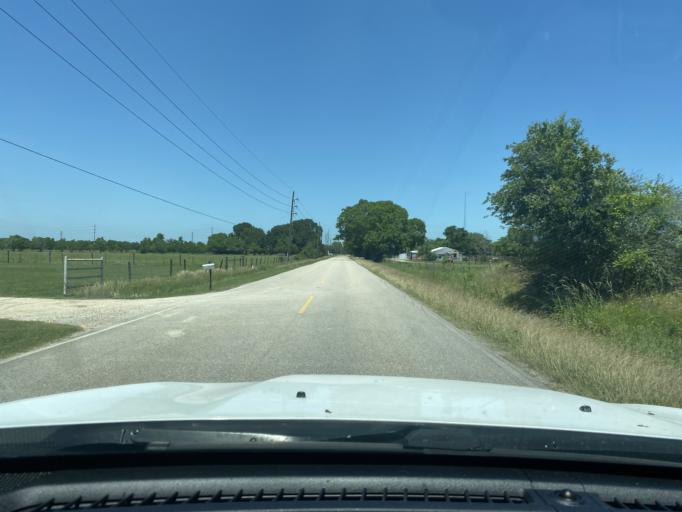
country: US
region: Texas
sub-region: Waller County
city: Waller
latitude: 30.0126
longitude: -95.8486
